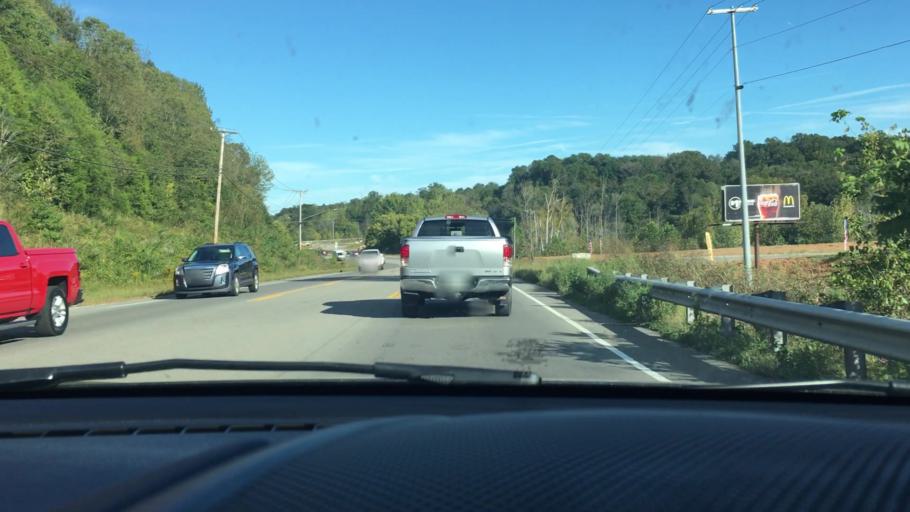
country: US
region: Tennessee
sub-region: Montgomery County
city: Clarksville
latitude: 36.5003
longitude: -87.2950
